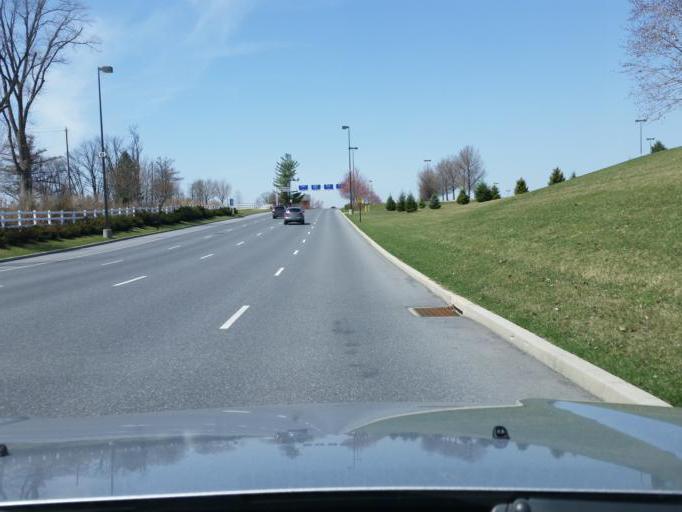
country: US
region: Pennsylvania
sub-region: Dauphin County
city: Hershey
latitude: 40.2829
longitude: -76.6713
